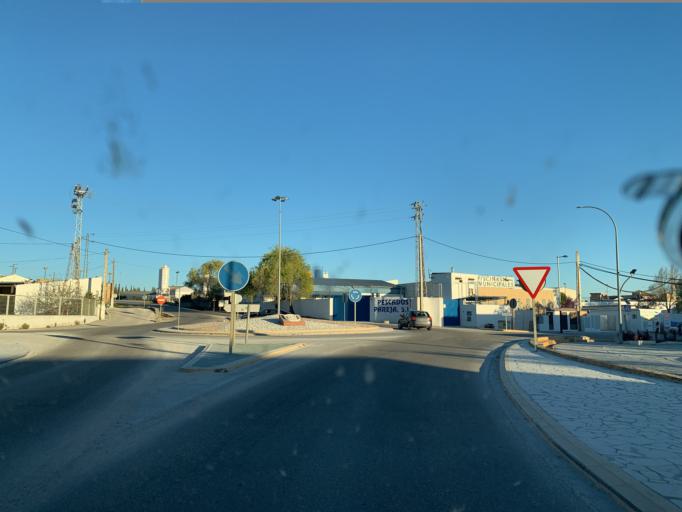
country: ES
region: Andalusia
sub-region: Provincia de Sevilla
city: Pedrera
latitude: 37.2300
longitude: -4.8932
